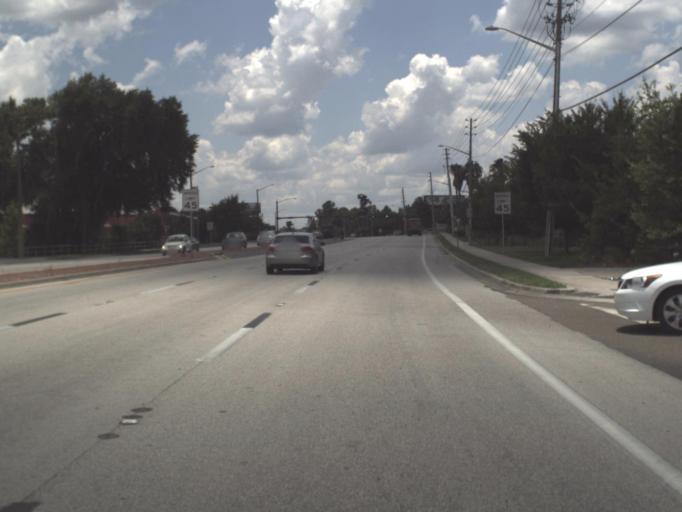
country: US
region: Florida
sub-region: Alachua County
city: Gainesville
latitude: 29.6242
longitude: -82.3726
